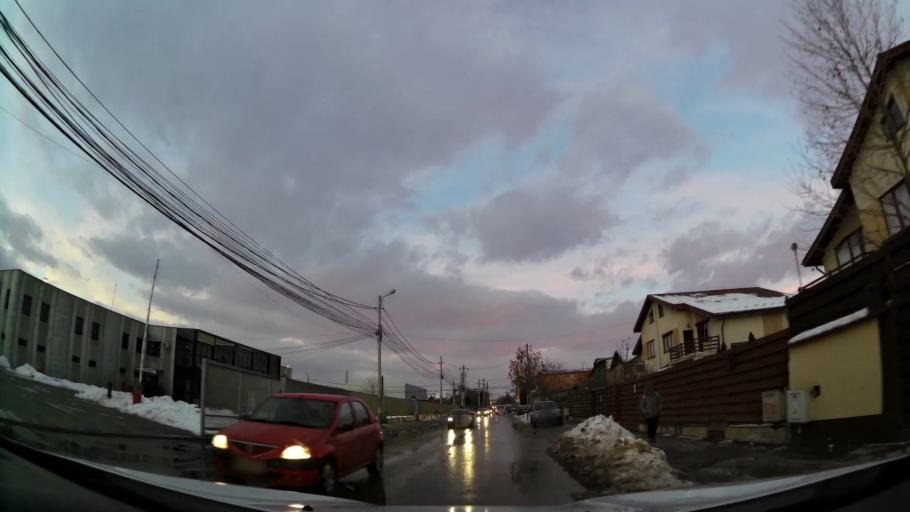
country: RO
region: Ilfov
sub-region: Comuna Popesti-Leordeni
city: Popesti-Leordeni
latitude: 44.3746
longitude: 26.1558
